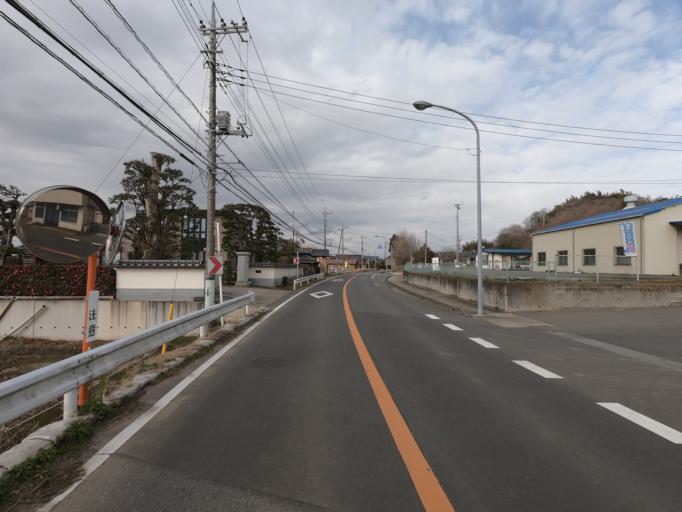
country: JP
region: Ibaraki
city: Inashiki
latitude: 36.0836
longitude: 140.4240
